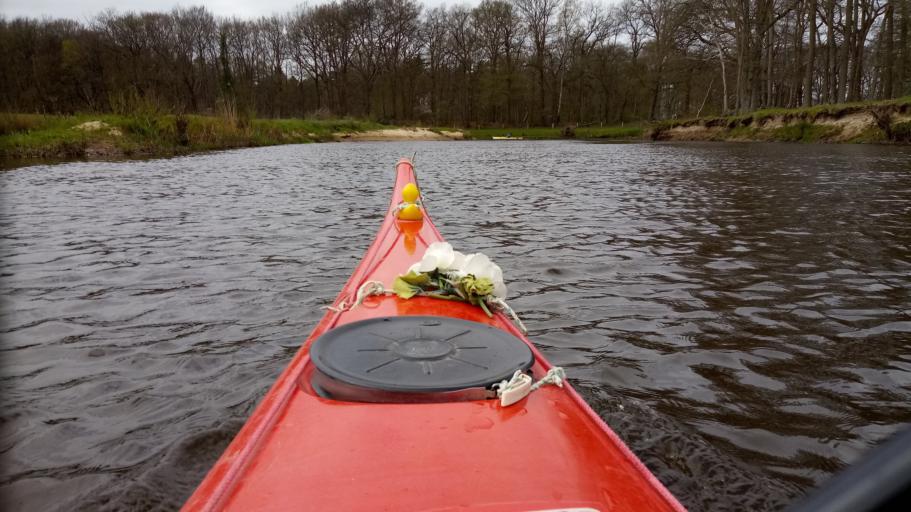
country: NL
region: Overijssel
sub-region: Gemeente Twenterand
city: Den Ham
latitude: 52.4889
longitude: 6.4361
